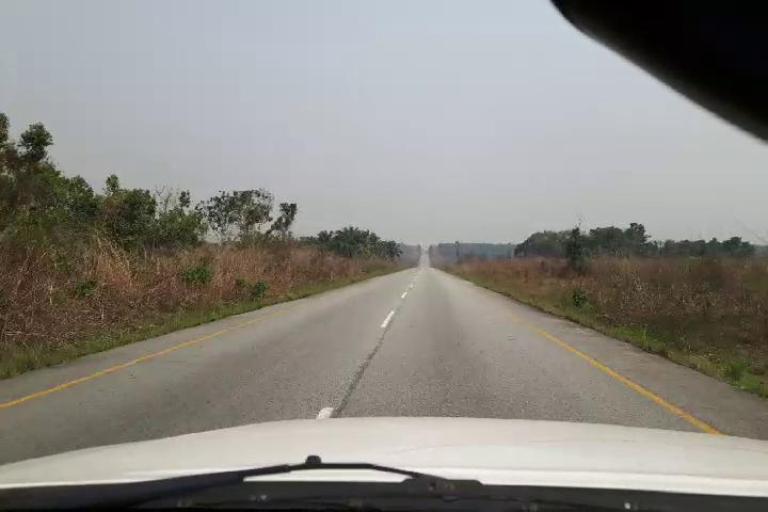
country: SL
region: Southern Province
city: Largo
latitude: 8.2371
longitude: -12.0831
